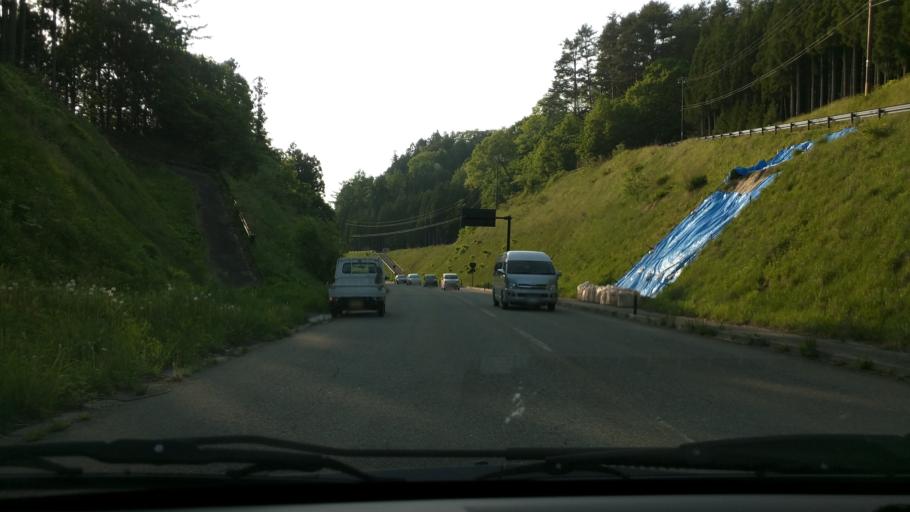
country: JP
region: Tochigi
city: Kuroiso
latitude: 37.2186
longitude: 139.9009
